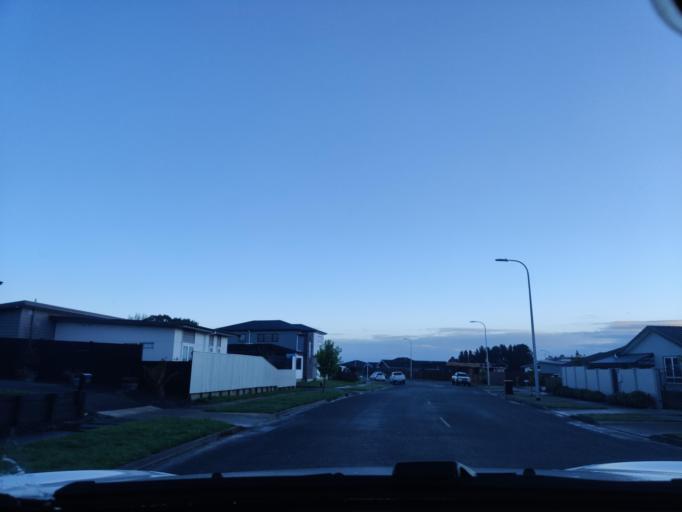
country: NZ
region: Manawatu-Wanganui
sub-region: Palmerston North City
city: Palmerston North
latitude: -40.3859
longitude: 175.6471
